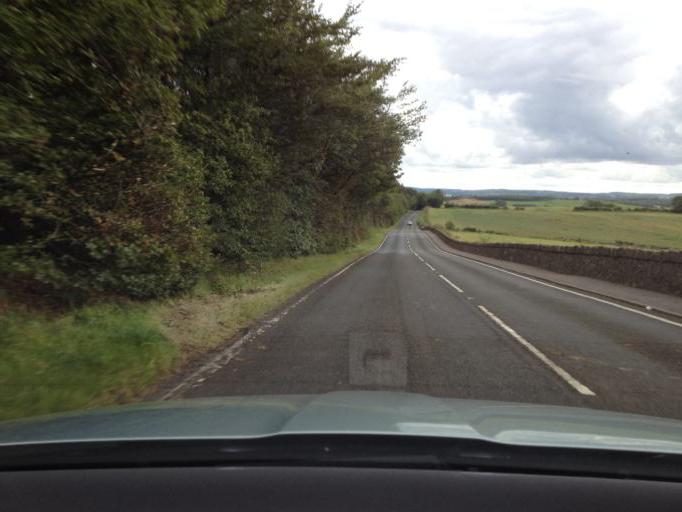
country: GB
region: Scotland
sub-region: West Lothian
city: Bathgate
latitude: 55.9290
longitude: -3.6483
